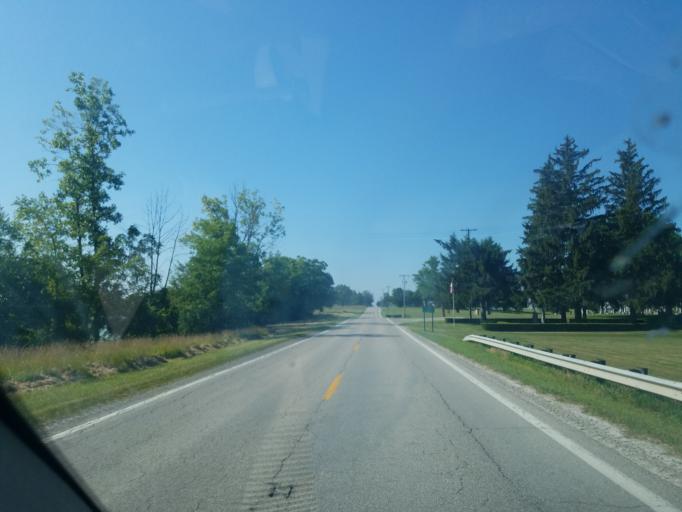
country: US
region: Ohio
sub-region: Union County
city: Richwood
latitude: 40.4137
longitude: -83.4529
